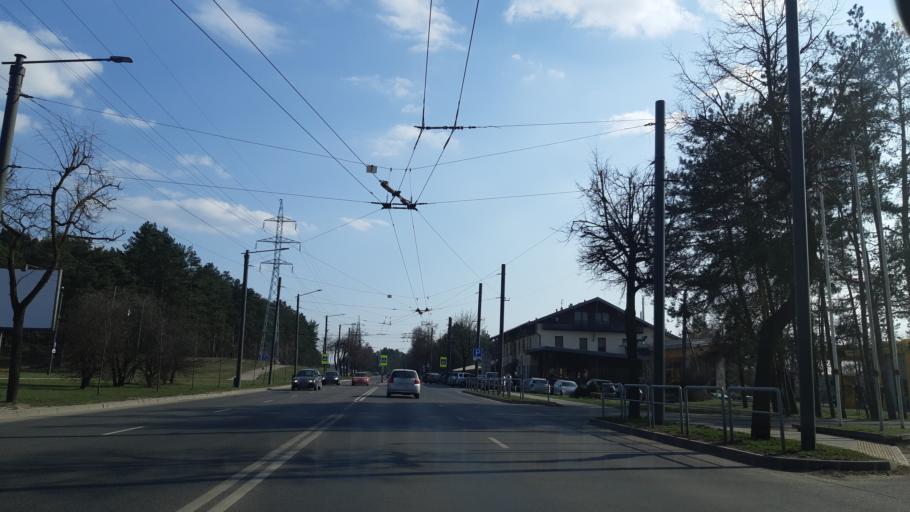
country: LT
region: Kauno apskritis
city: Dainava (Kaunas)
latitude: 54.8853
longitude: 24.0070
